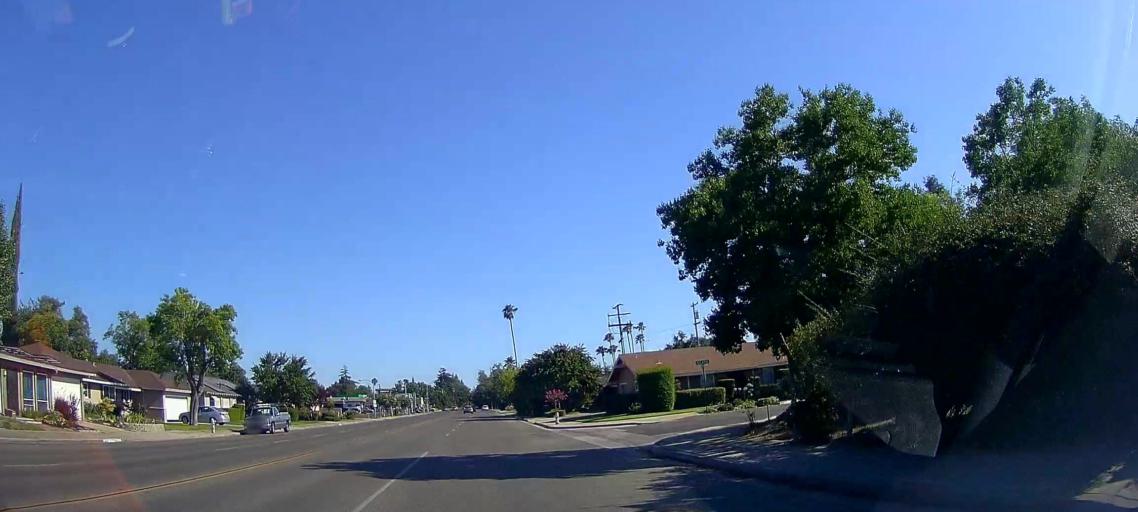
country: US
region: California
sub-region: Fresno County
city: Fresno
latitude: 36.8104
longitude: -119.7995
